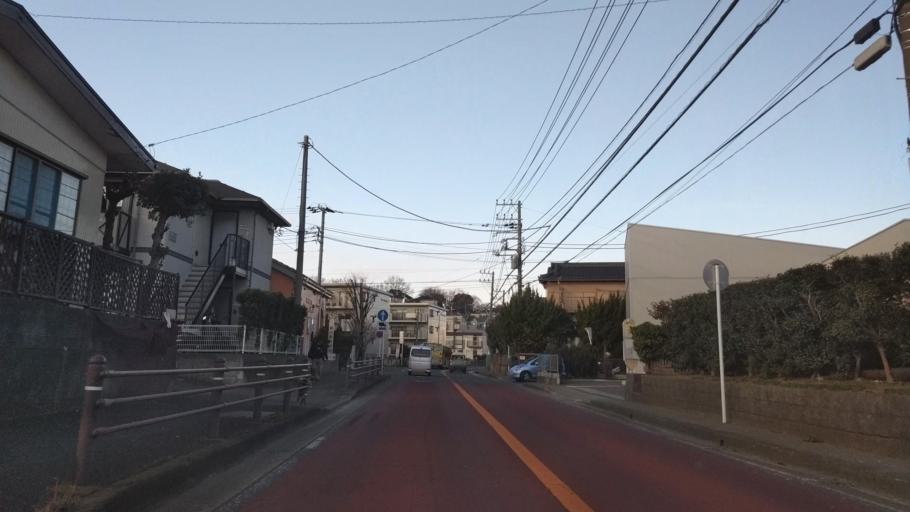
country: JP
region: Kanagawa
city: Isehara
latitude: 35.3516
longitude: 139.3018
